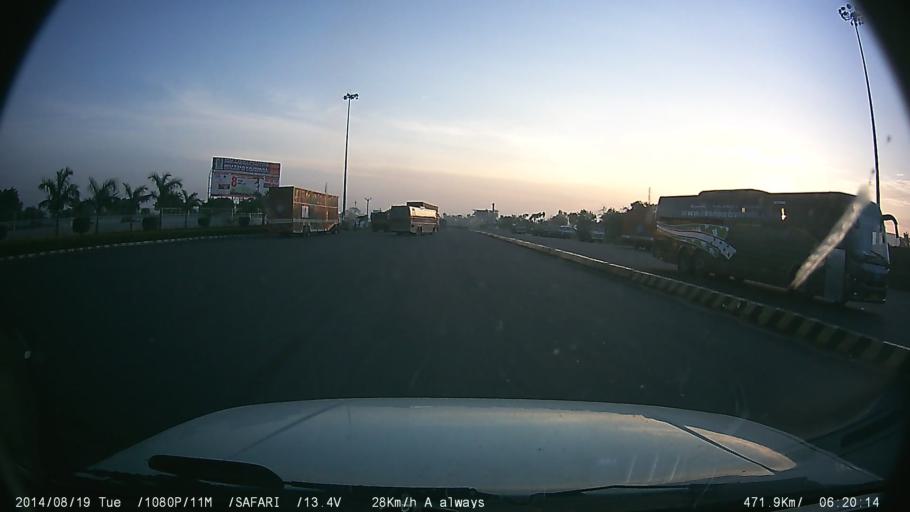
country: IN
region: Tamil Nadu
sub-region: Dharmapuri
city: Dharmapuri
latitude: 12.0068
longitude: 78.0808
